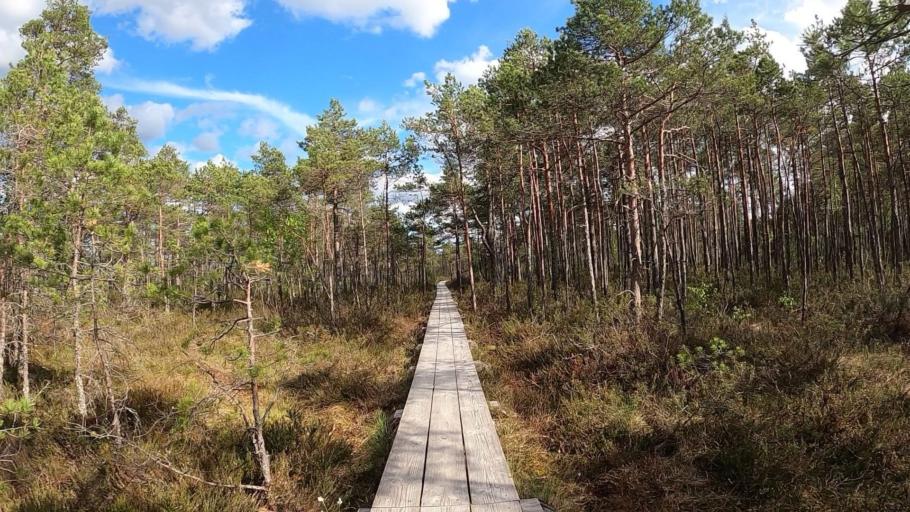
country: LV
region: Jurmala
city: Jurmala
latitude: 56.8550
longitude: 23.8111
